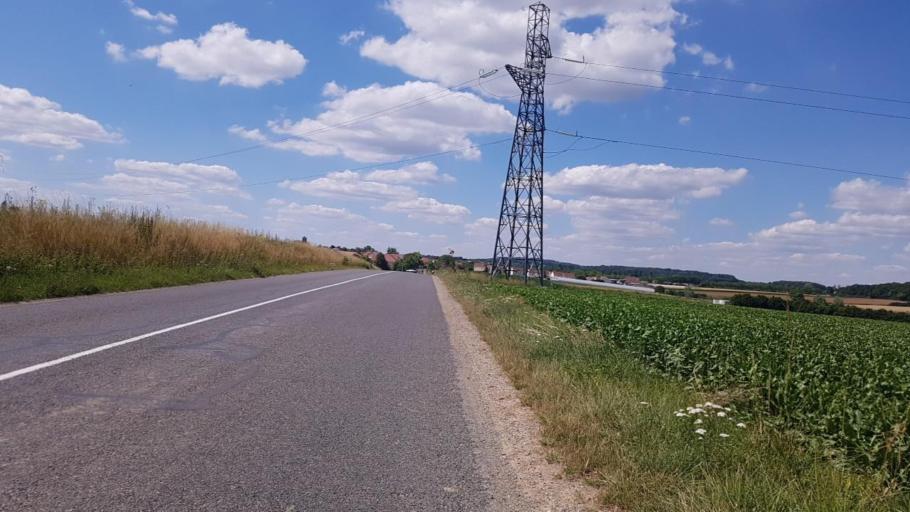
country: FR
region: Ile-de-France
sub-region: Departement de Seine-et-Marne
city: Moussy-le-Neuf
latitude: 49.0571
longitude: 2.6145
